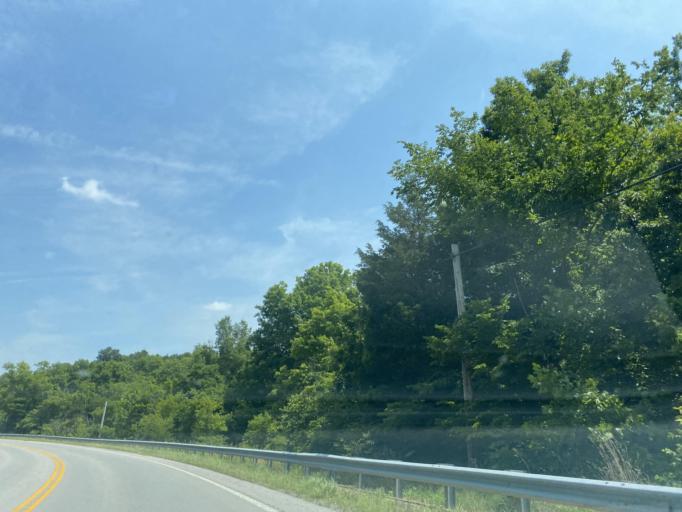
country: US
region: Kentucky
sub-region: Campbell County
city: Claryville
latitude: 38.9282
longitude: -84.4265
